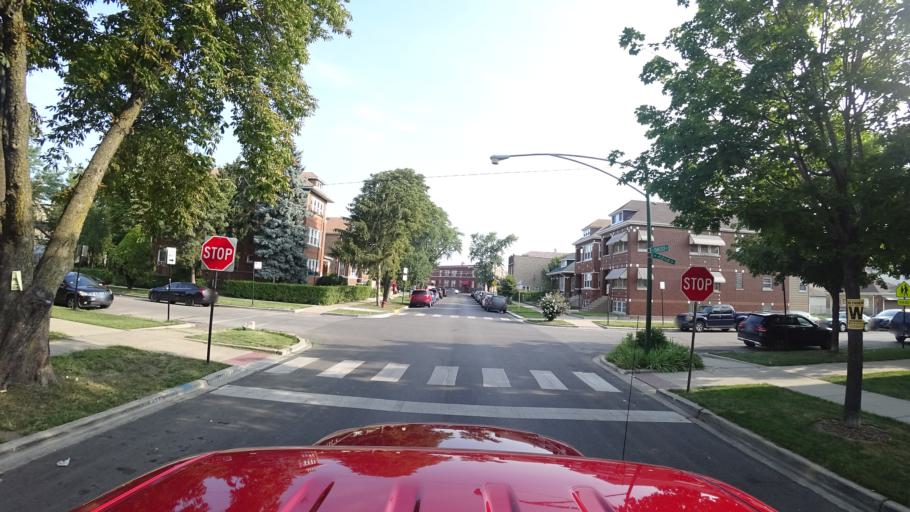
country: US
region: Illinois
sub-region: Cook County
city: Chicago
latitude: 41.8171
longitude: -87.6970
